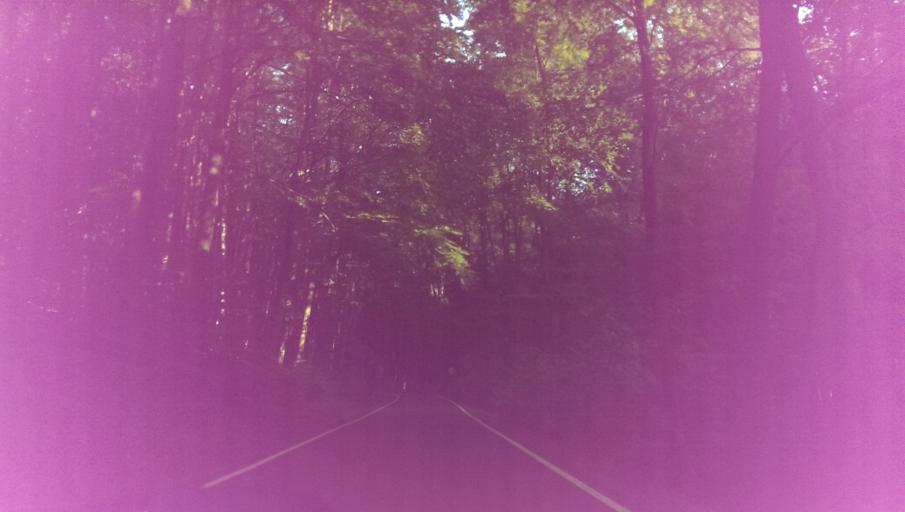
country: CZ
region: Zlin
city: Korycany
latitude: 49.0893
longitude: 17.2106
